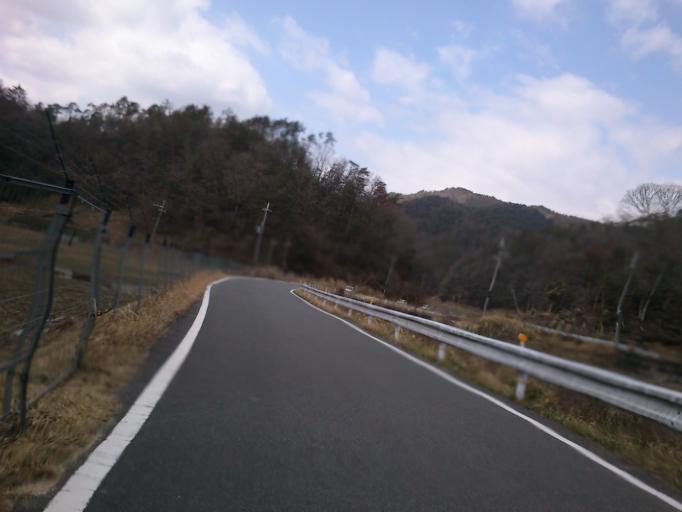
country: JP
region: Mie
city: Ueno-ebisumachi
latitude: 34.8315
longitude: 135.9816
